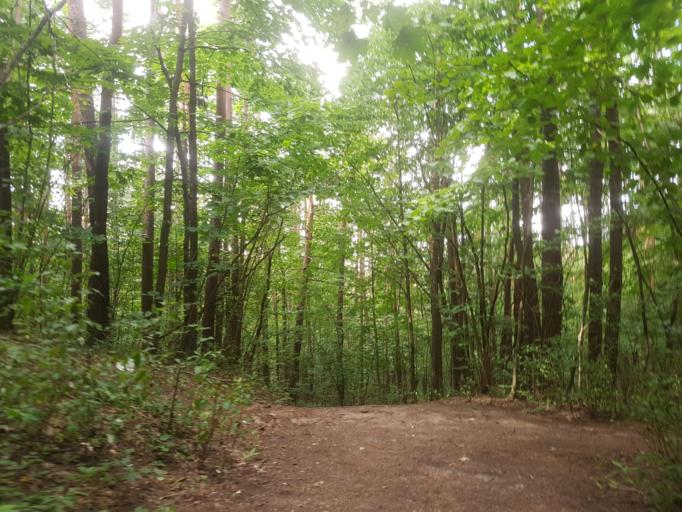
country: LT
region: Vilnius County
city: Rasos
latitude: 54.7839
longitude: 25.3376
